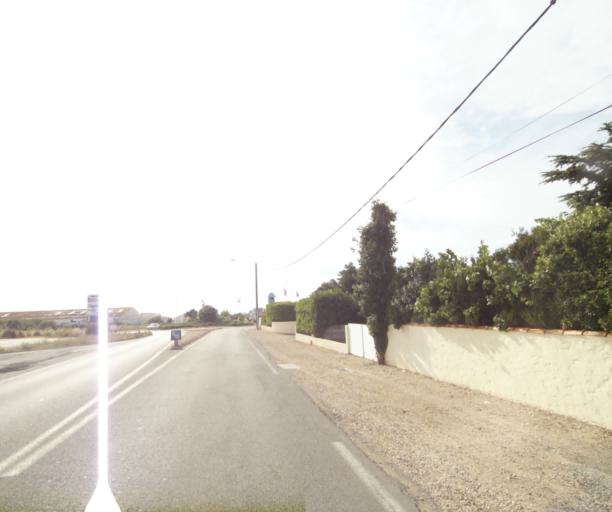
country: FR
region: Pays de la Loire
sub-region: Departement de la Vendee
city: Chateau-d'Olonne
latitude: 46.4863
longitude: -1.7373
